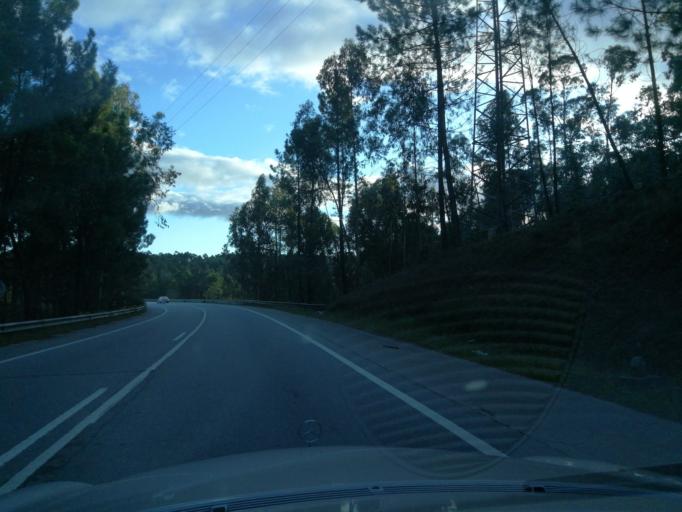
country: PT
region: Braga
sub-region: Barcelos
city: Vila Frescainha
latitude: 41.5482
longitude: -8.6519
